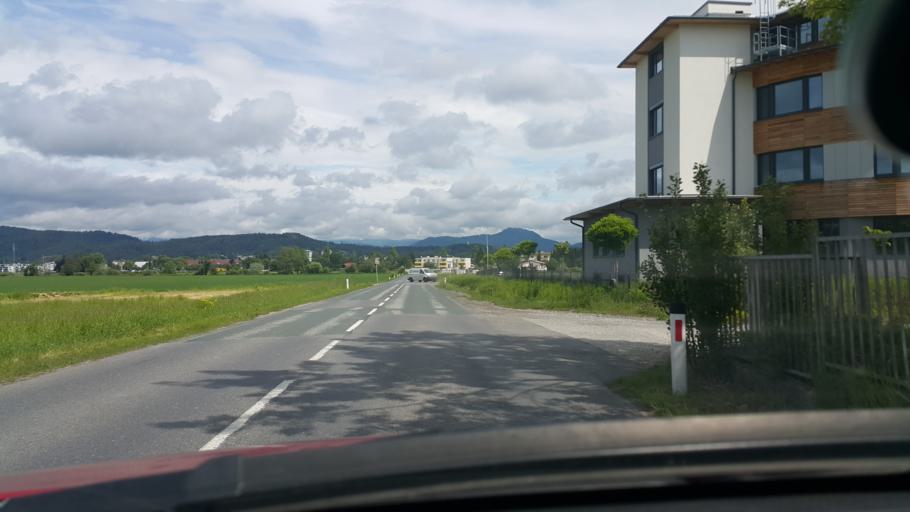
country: AT
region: Carinthia
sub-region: Klagenfurt am Woerthersee
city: Klagenfurt am Woerthersee
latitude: 46.5994
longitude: 14.2900
